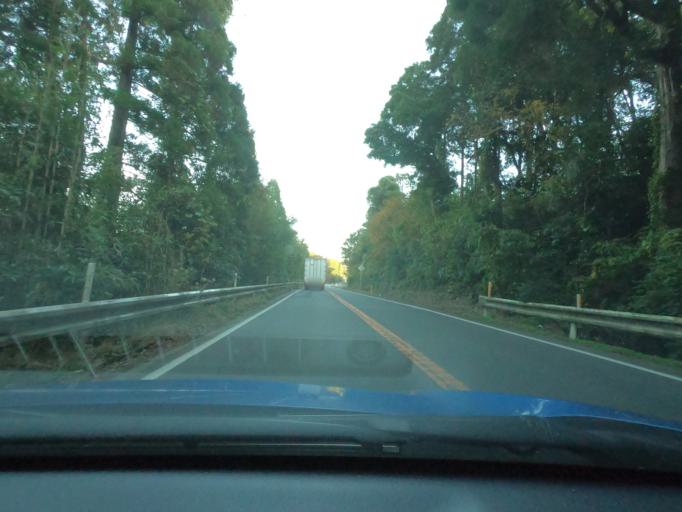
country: JP
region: Kagoshima
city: Satsumasendai
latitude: 31.8438
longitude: 130.2772
